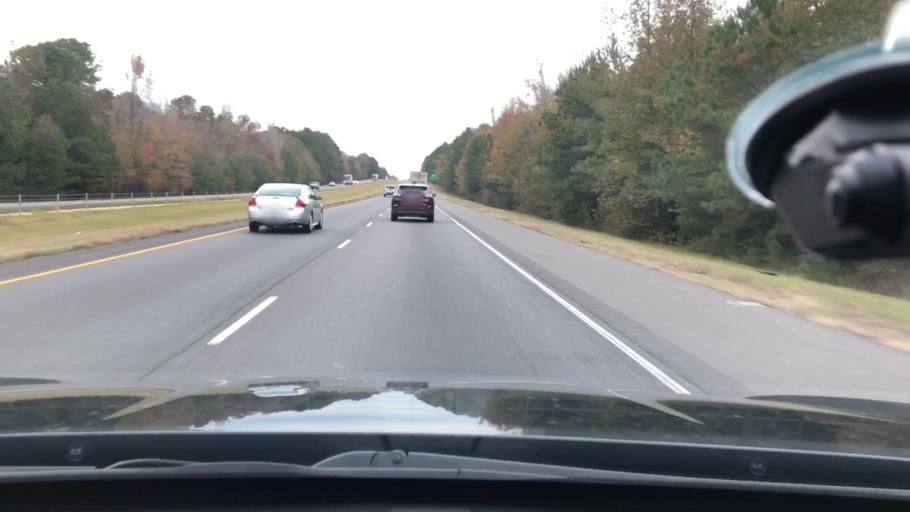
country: US
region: Arkansas
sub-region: Clark County
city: Arkadelphia
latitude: 34.0527
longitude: -93.1328
